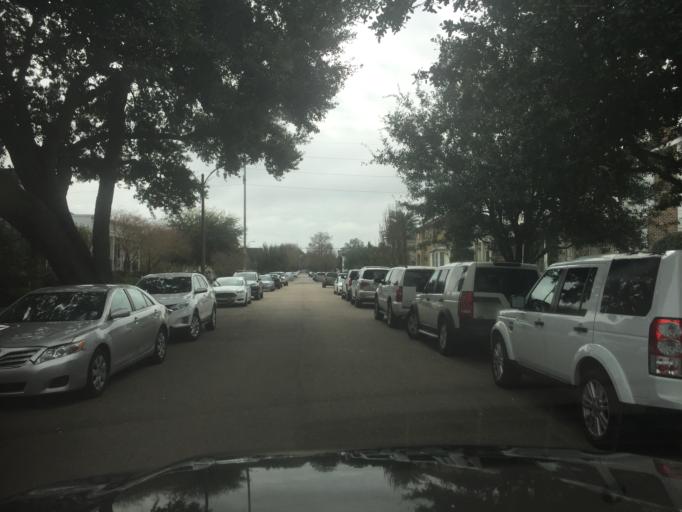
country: US
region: Louisiana
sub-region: Jefferson Parish
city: Metairie
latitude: 30.0018
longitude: -90.1071
